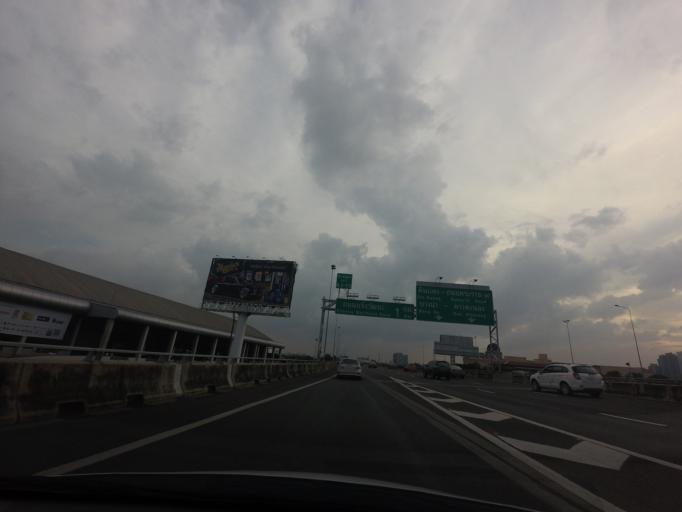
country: TH
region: Bangkok
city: Lak Si
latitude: 13.9132
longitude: 100.5450
